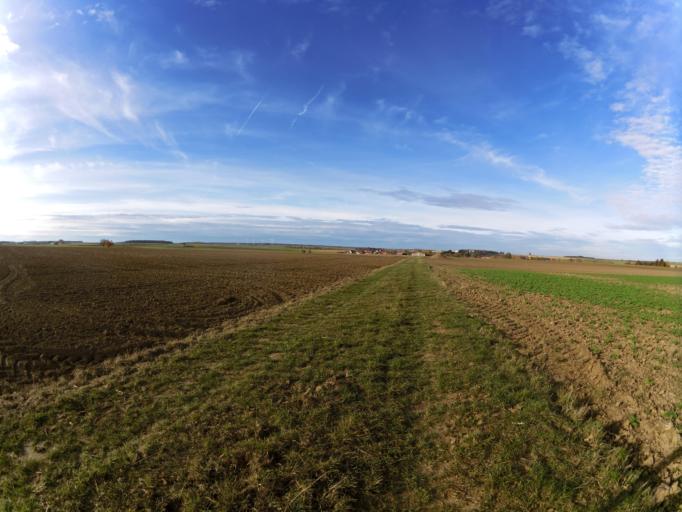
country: DE
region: Bavaria
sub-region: Regierungsbezirk Unterfranken
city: Giebelstadt
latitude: 49.6623
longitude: 9.9626
